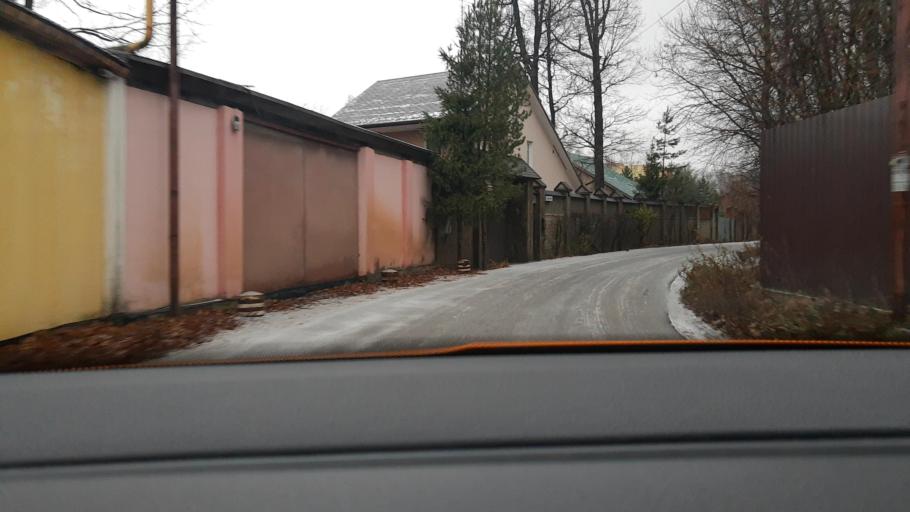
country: RU
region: Moscow
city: Severnyy
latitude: 55.9579
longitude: 37.5597
